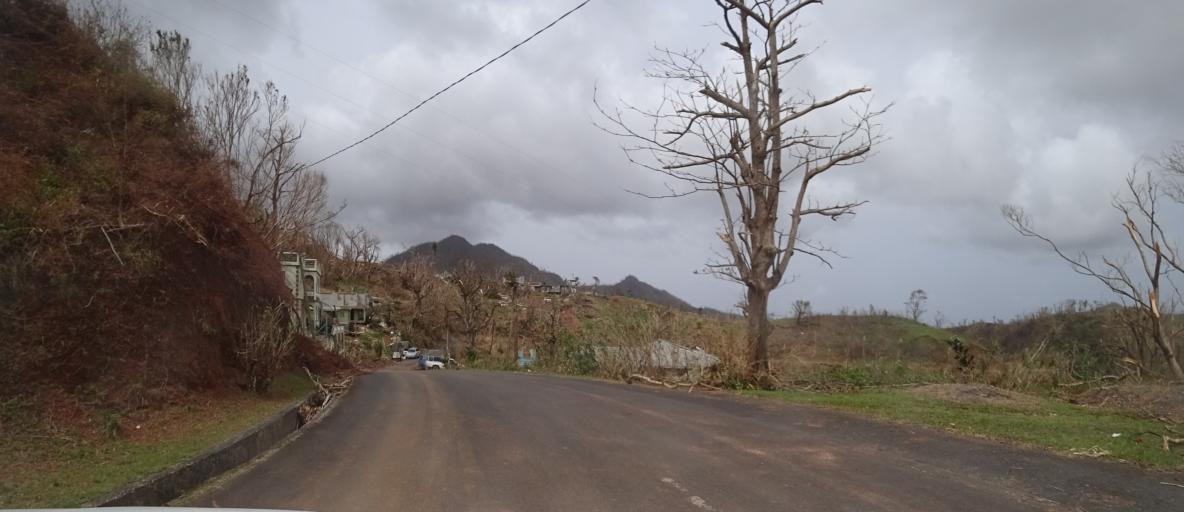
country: DM
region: Saint John
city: Portsmouth
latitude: 15.5780
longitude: -61.4196
